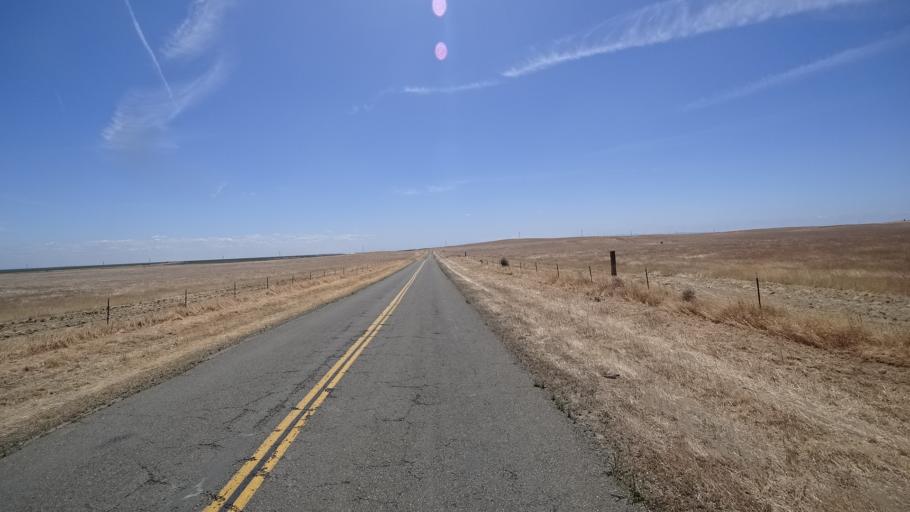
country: US
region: California
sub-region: Kings County
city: Kettleman City
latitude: 35.8017
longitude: -119.8958
